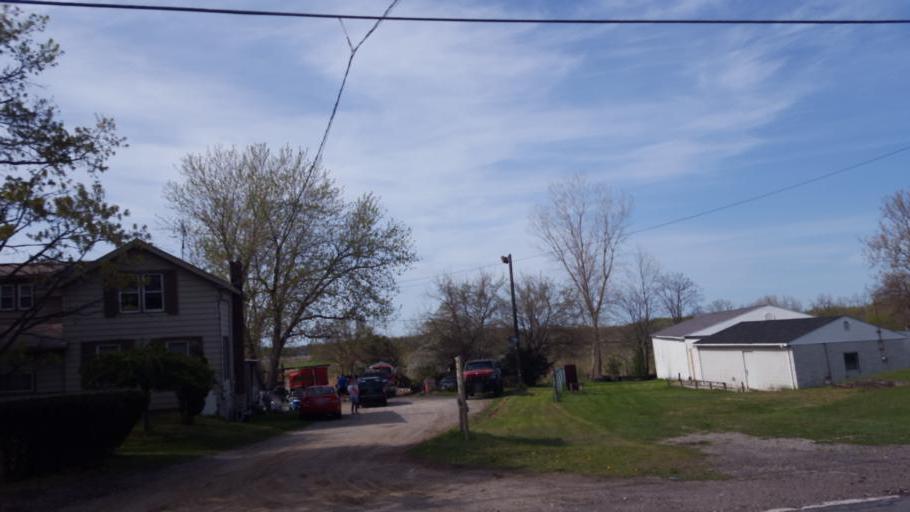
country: US
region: Ohio
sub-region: Lake County
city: Perry
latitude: 41.7764
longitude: -81.1585
